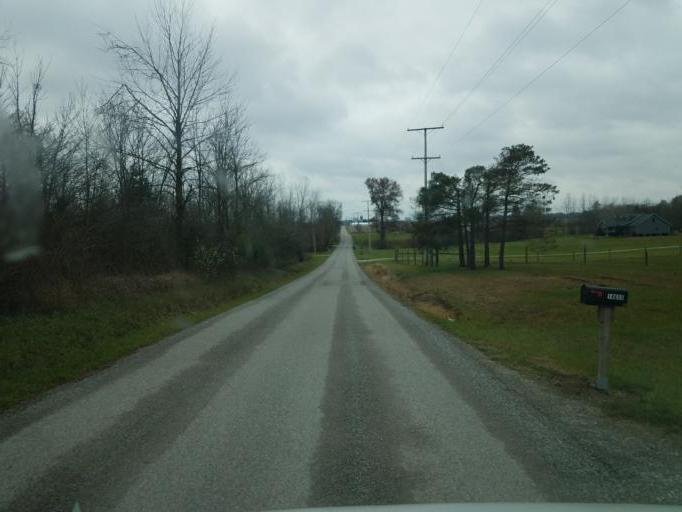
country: US
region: Ohio
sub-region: Knox County
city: Centerburg
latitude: 40.2614
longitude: -82.6404
